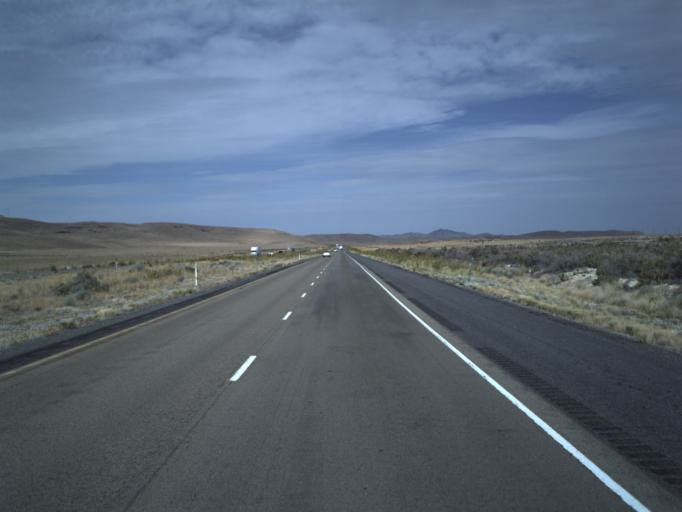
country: US
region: Utah
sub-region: Tooele County
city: Grantsville
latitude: 40.7872
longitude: -112.8256
